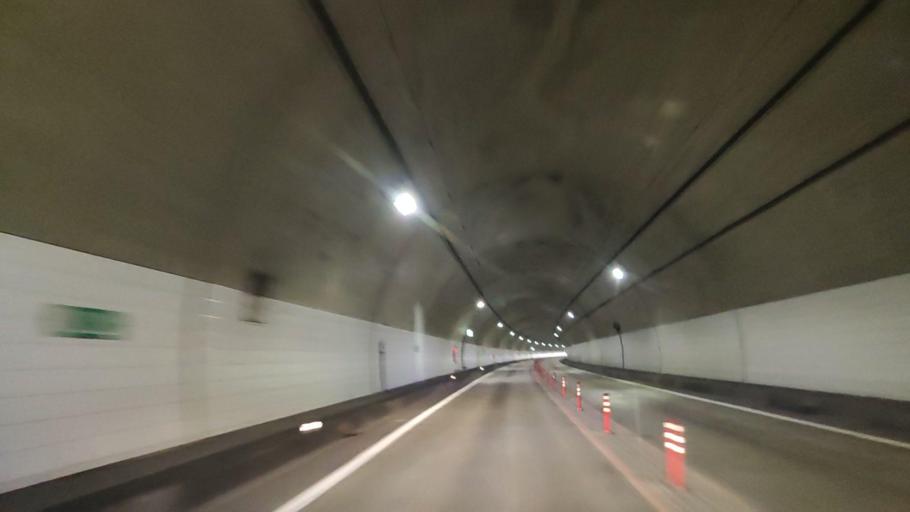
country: JP
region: Akita
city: Odate
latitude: 40.3608
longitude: 140.6945
